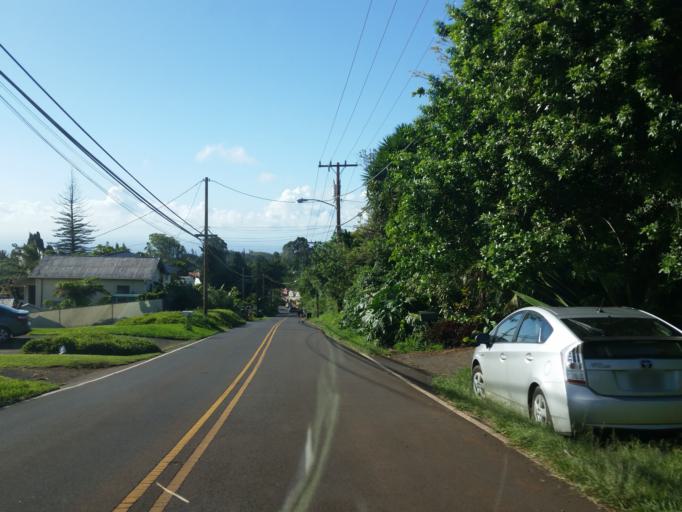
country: US
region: Hawaii
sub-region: Maui County
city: Makawao
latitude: 20.8520
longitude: -156.3093
